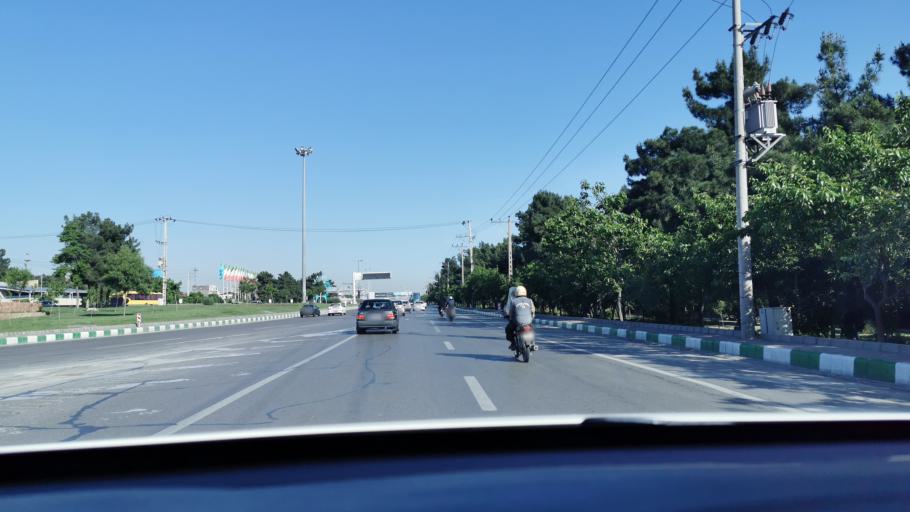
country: IR
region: Razavi Khorasan
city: Mashhad
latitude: 36.2519
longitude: 59.6074
